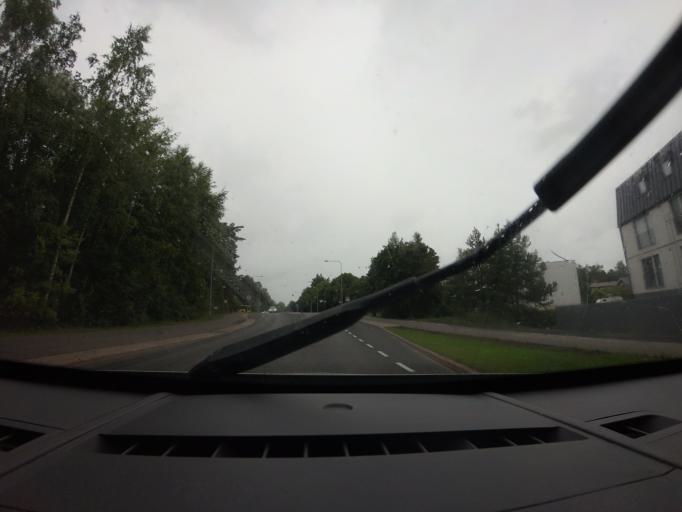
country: FI
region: Varsinais-Suomi
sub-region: Turku
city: Turku
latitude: 60.4271
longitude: 22.2923
